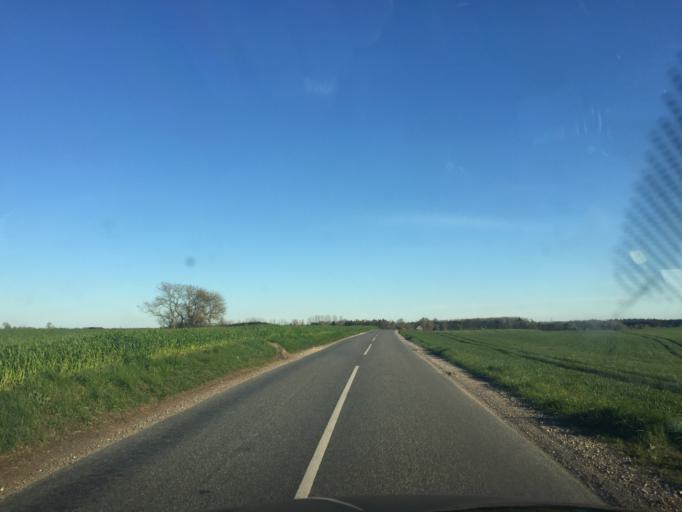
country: DK
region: Capital Region
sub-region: Egedal Kommune
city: Vekso
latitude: 55.7249
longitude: 12.2403
